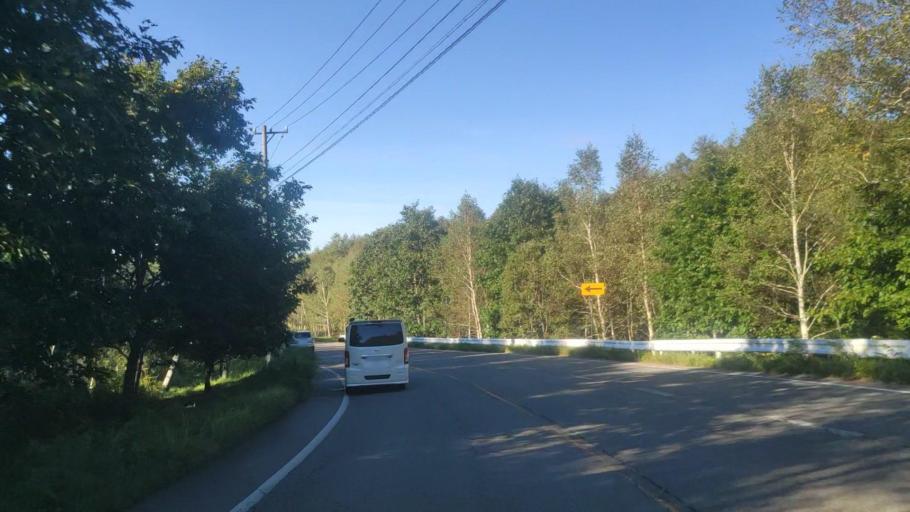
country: JP
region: Nagano
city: Kamimaruko
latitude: 36.1614
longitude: 138.2811
